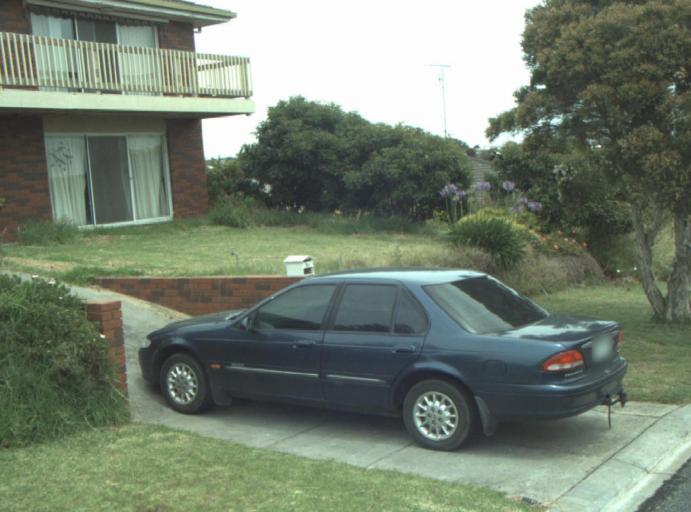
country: AU
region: Victoria
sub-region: Greater Geelong
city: Clifton Springs
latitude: -38.1568
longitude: 144.5695
